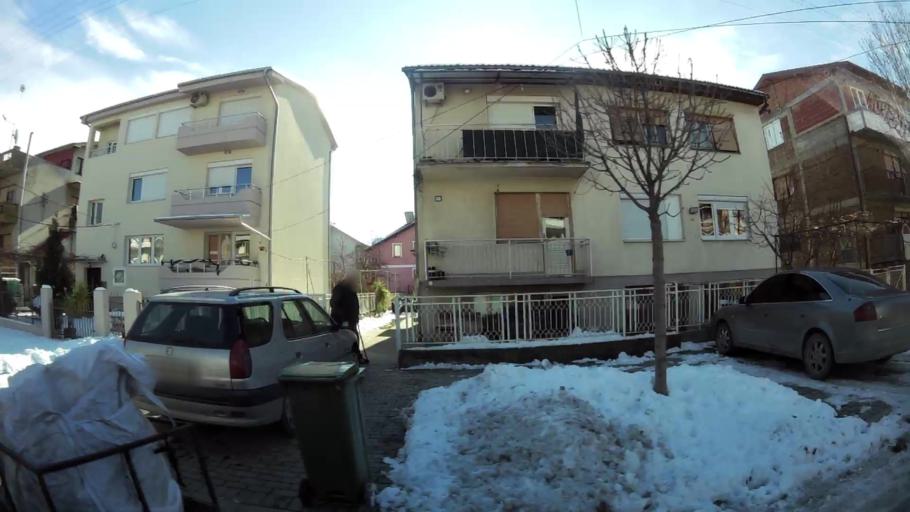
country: MK
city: Krushopek
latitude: 42.0049
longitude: 21.3562
